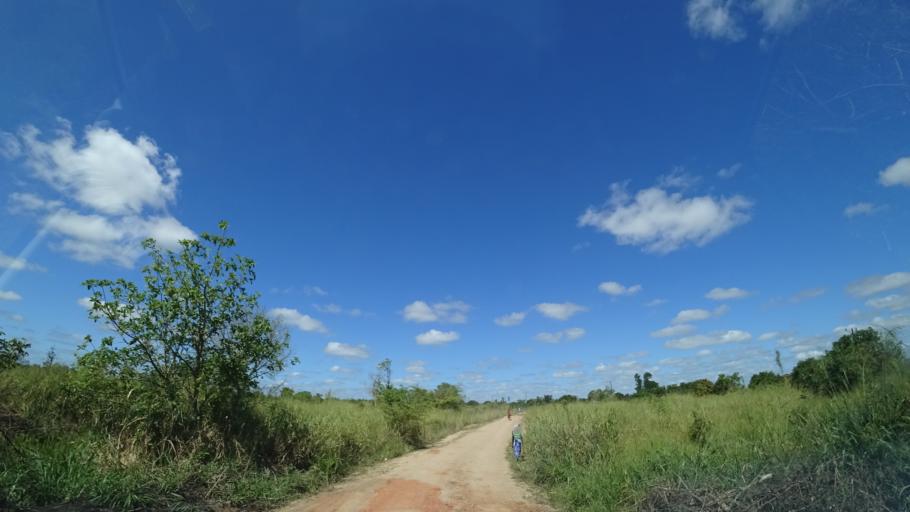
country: MZ
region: Sofala
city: Dondo
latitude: -19.2744
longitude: 34.6806
